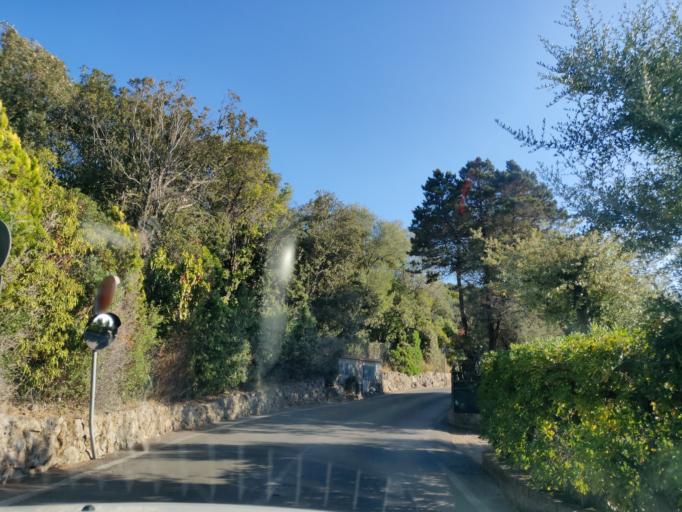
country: IT
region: Tuscany
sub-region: Provincia di Grosseto
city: Orbetello Scalo
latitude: 42.4143
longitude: 11.2811
